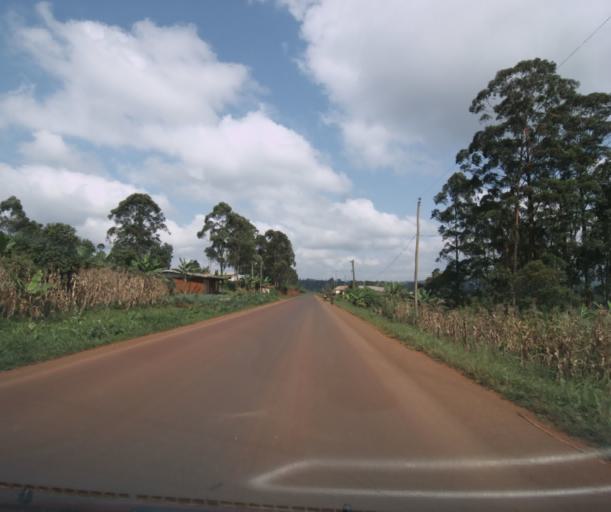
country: CM
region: West
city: Dschang
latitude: 5.4894
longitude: 10.1763
